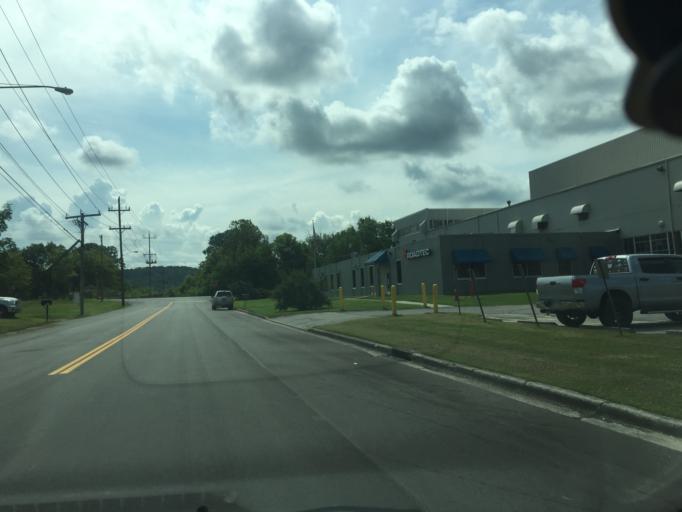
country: US
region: Tennessee
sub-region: Hamilton County
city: East Chattanooga
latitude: 35.0753
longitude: -85.2598
